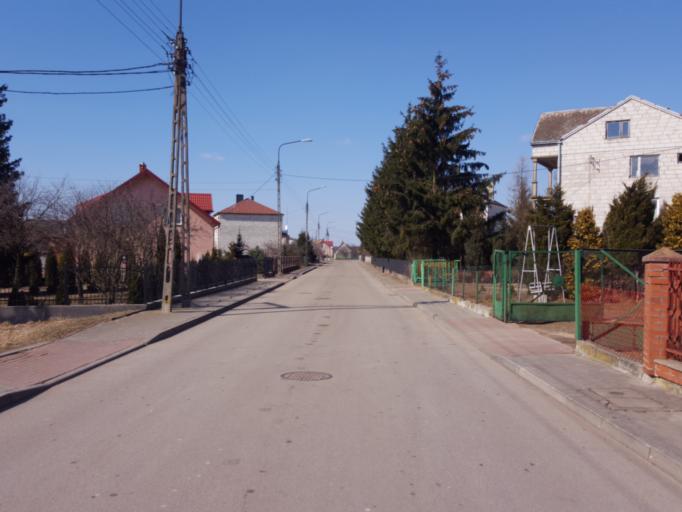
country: PL
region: Podlasie
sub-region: Powiat kolnenski
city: Stawiski
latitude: 53.3762
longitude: 22.1527
